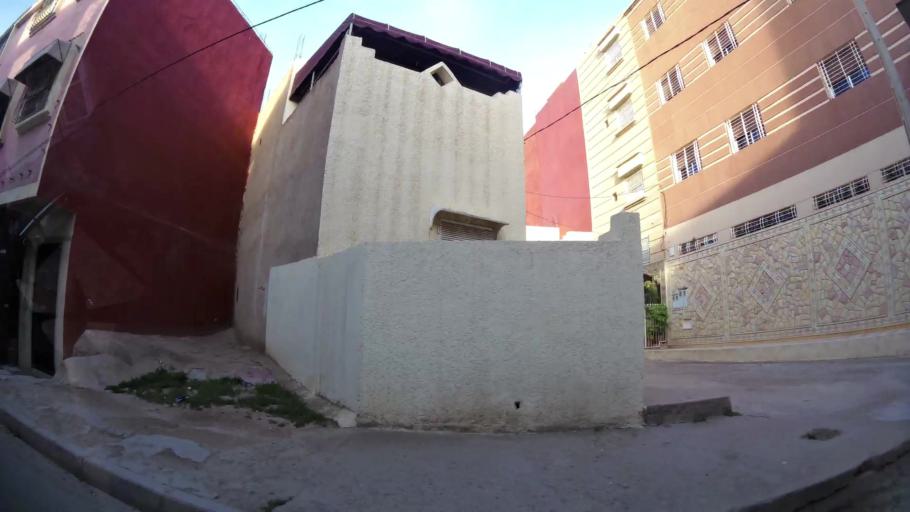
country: MA
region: Oriental
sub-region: Oujda-Angad
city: Oujda
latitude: 34.6781
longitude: -1.9002
